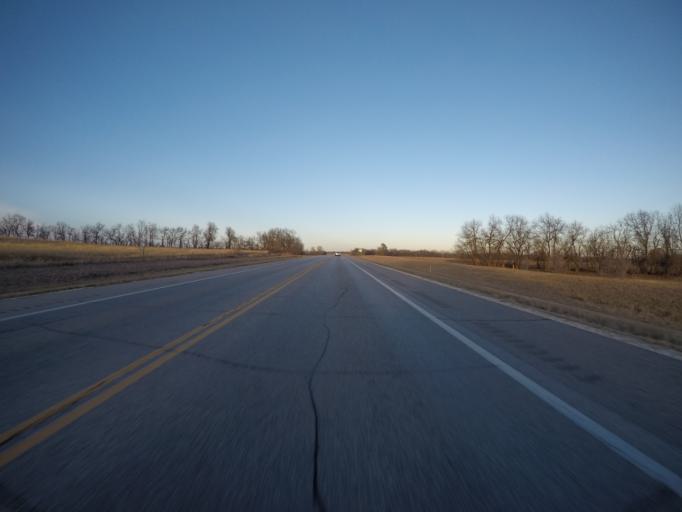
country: US
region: Kansas
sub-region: Marion County
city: Peabody
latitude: 38.1659
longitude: -97.2003
